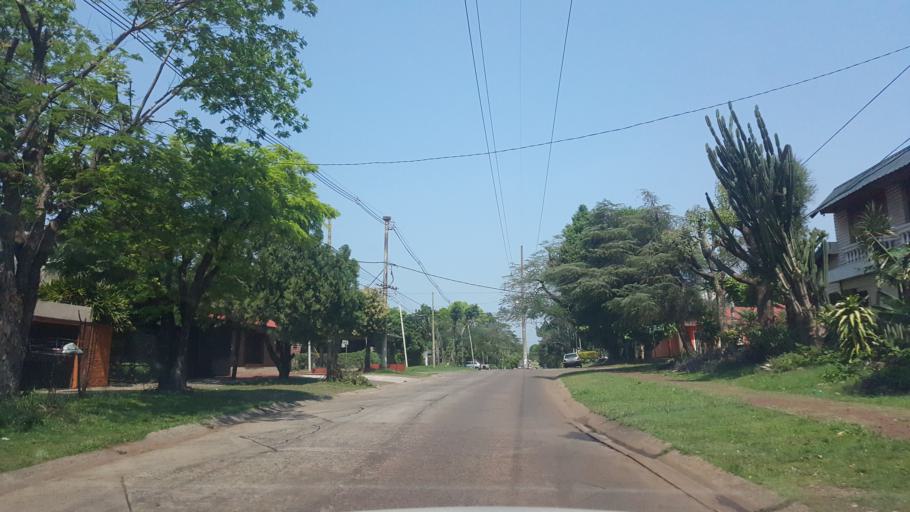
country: AR
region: Misiones
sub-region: Departamento de Capital
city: Posadas
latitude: -27.3697
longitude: -55.9131
